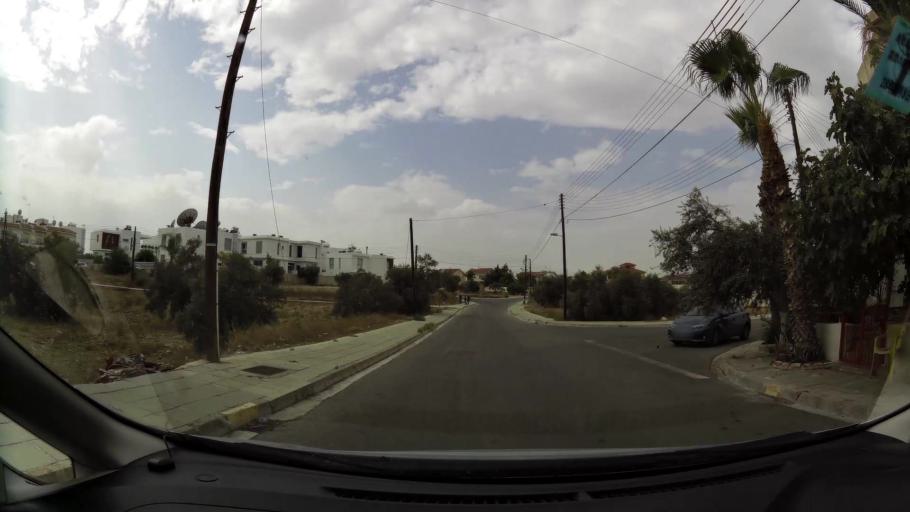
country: CY
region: Lefkosia
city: Geri
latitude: 35.0990
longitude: 33.3763
